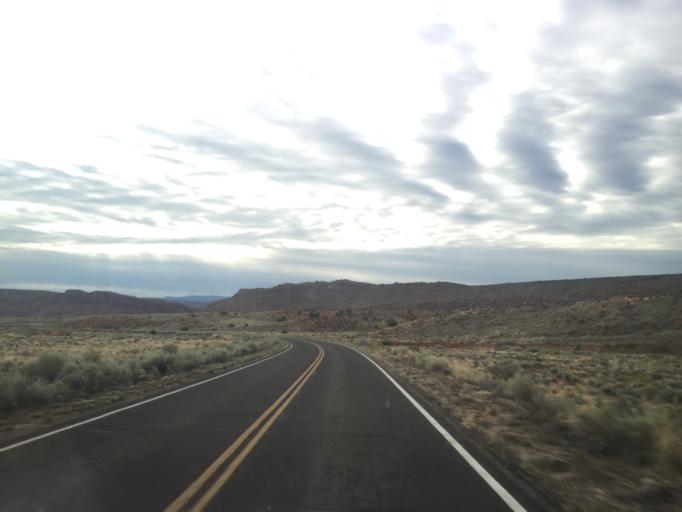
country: US
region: Utah
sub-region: Grand County
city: Moab
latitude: 38.7337
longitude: -109.5574
